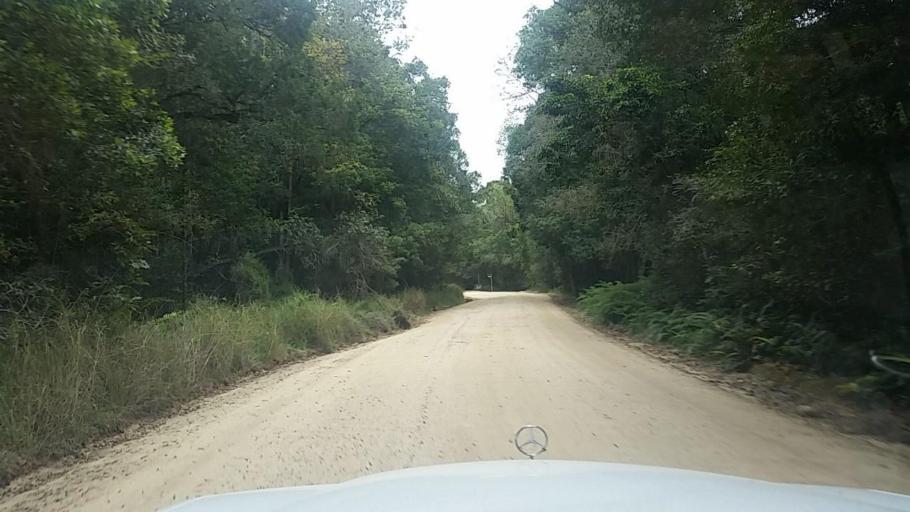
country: ZA
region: Western Cape
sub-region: Eden District Municipality
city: Knysna
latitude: -33.9494
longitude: 23.1497
